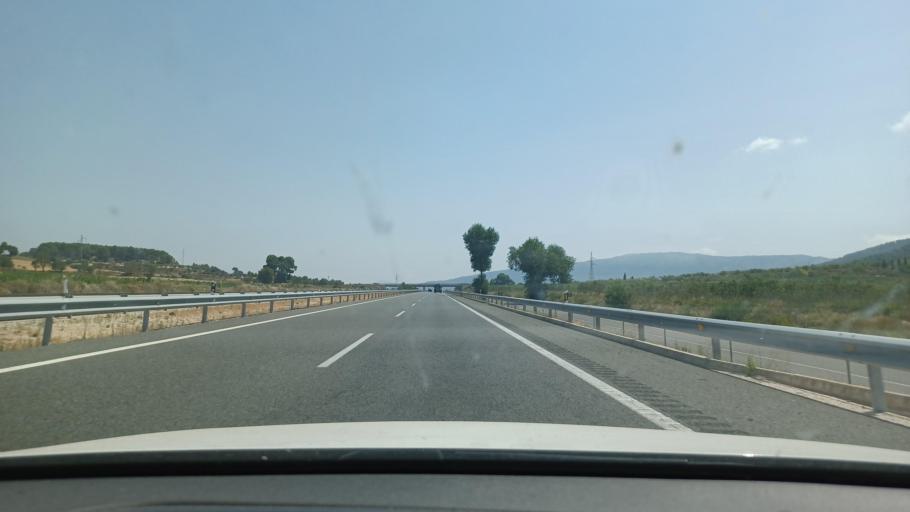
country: ES
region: Valencia
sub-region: Provincia de Alicante
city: Ibi
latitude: 38.6367
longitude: -0.5089
